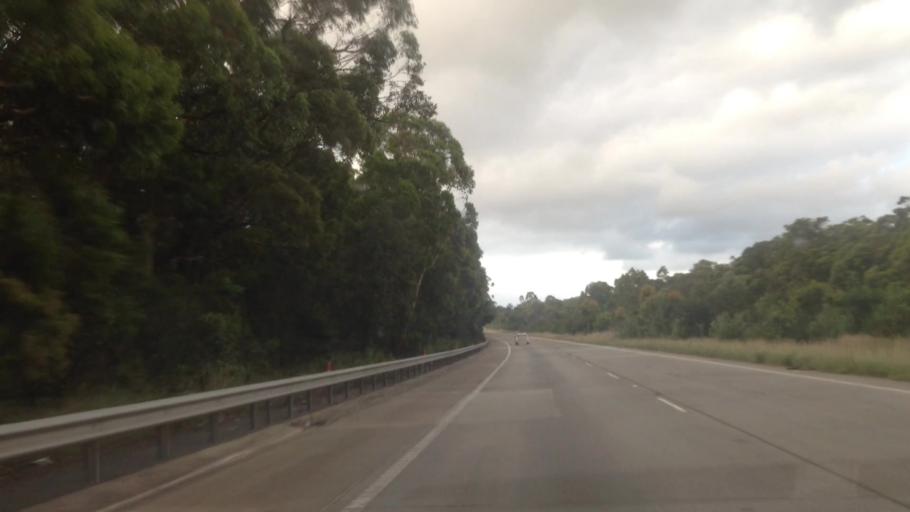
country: AU
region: New South Wales
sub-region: Wyong Shire
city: Charmhaven
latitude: -33.1881
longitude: 151.4675
